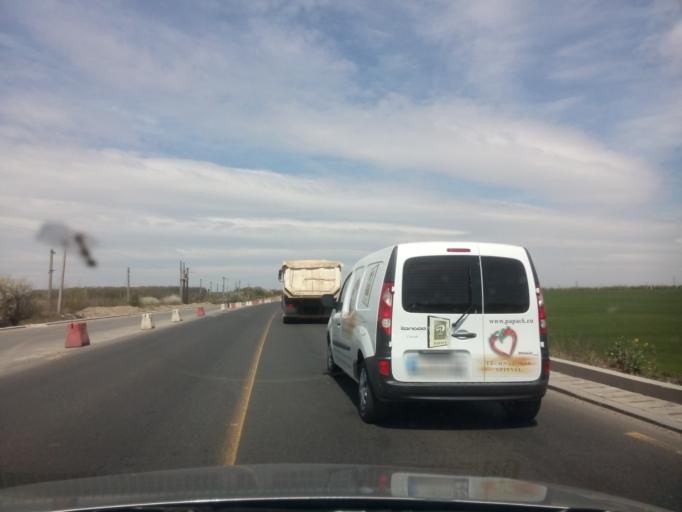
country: RO
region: Ilfov
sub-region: Comuna Pantelimon
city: Pantelimon
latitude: 44.4665
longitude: 26.2332
